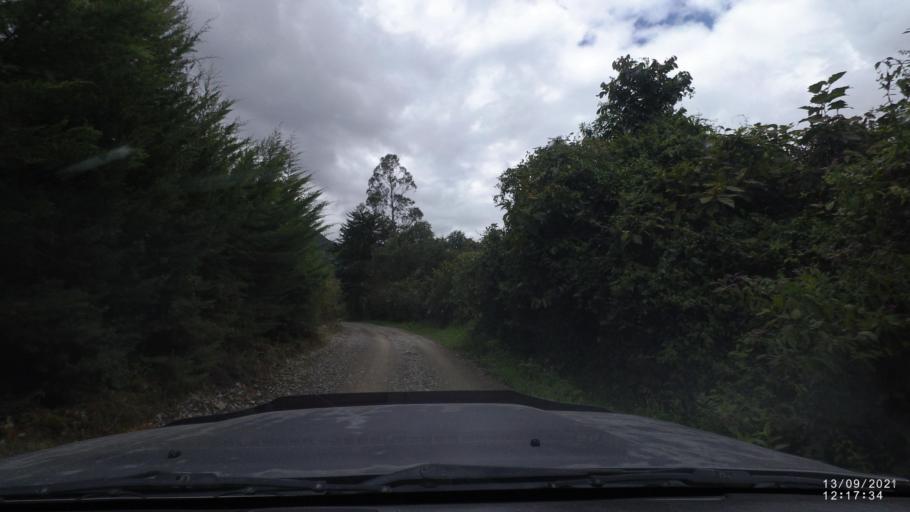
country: BO
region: Cochabamba
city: Colomi
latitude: -17.2280
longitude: -65.8185
